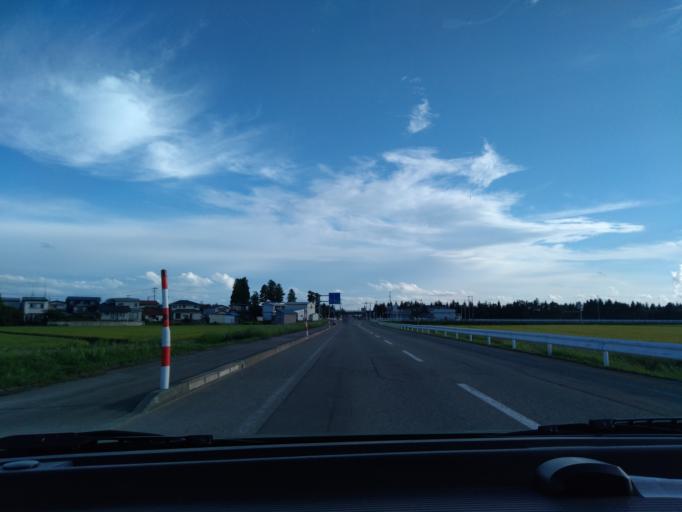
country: JP
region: Akita
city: Omagari
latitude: 39.4026
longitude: 140.4746
